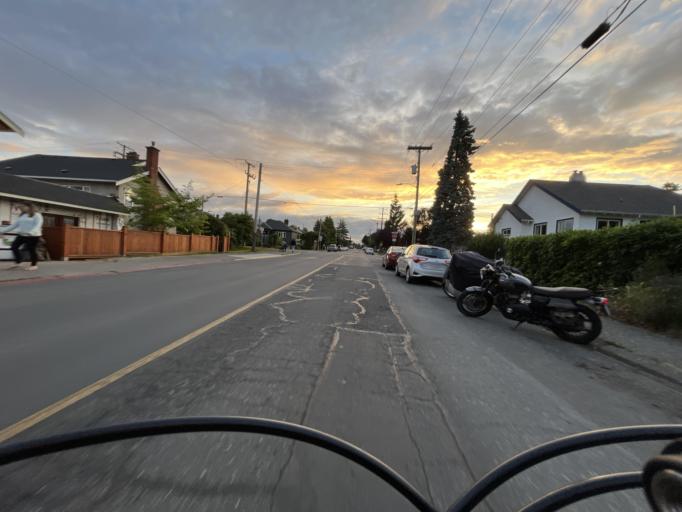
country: CA
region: British Columbia
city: Victoria
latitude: 48.4272
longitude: -123.4070
